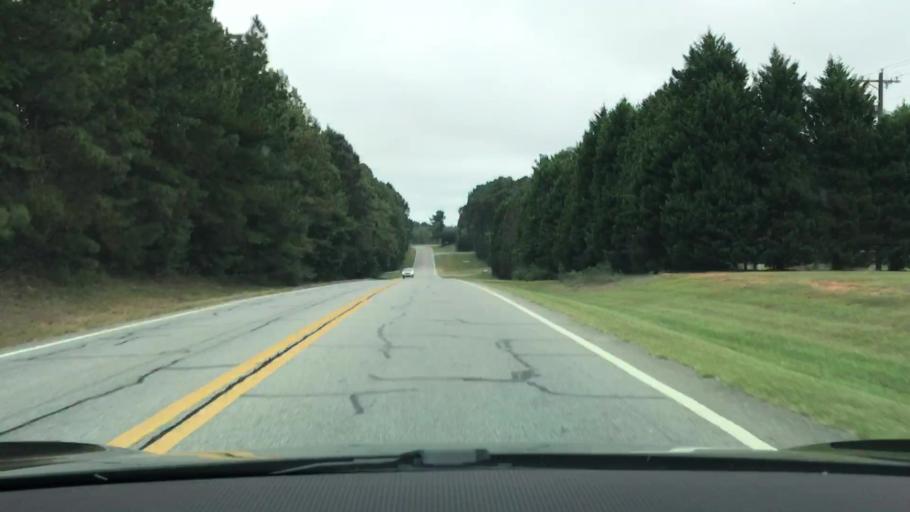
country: US
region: Georgia
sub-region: Oconee County
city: Watkinsville
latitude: 33.7754
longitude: -83.3109
